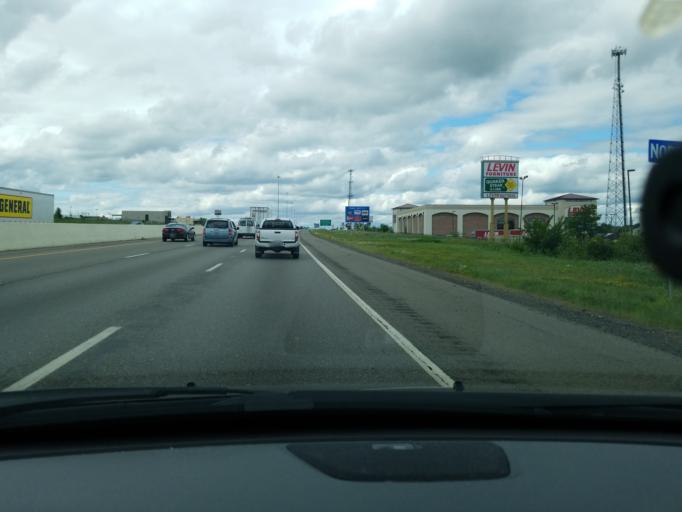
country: US
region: Ohio
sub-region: Stark County
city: North Canton
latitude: 40.8700
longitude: -81.4303
